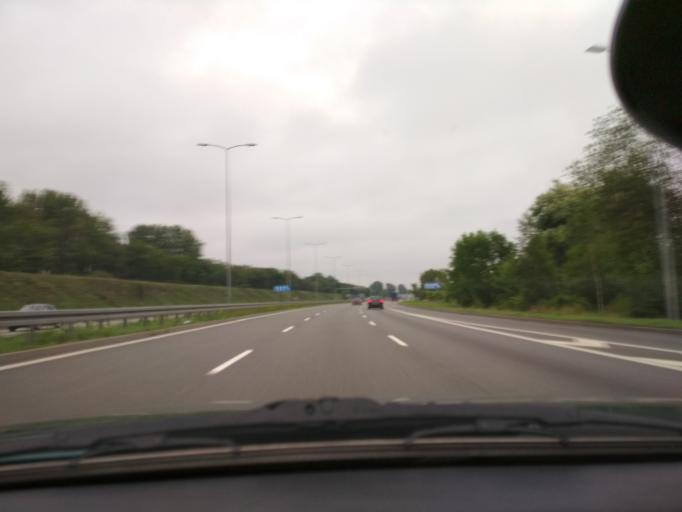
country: PL
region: Silesian Voivodeship
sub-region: Ruda Slaska
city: Ruda Slaska
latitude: 50.2978
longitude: 18.8351
